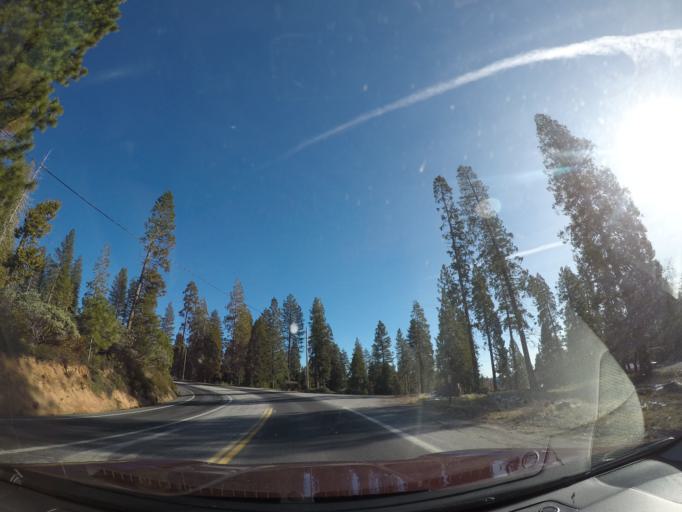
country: US
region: California
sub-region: Tuolumne County
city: Twain Harte
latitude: 38.0655
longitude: -120.1846
